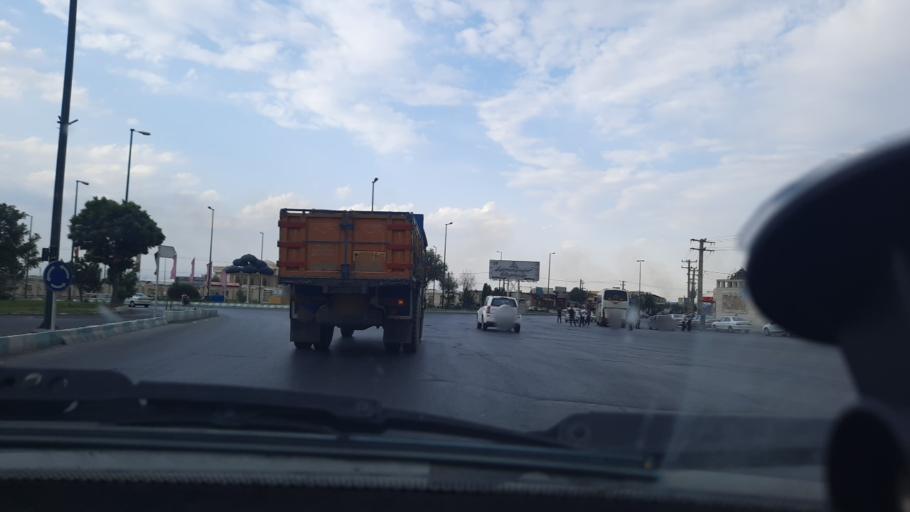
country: IR
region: Markazi
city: Arak
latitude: 34.0710
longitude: 49.7781
